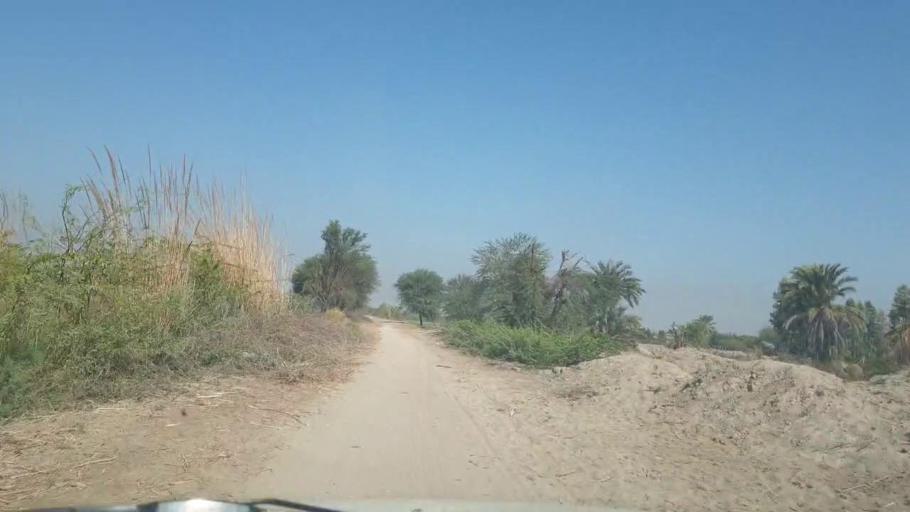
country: PK
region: Sindh
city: Mirpur Khas
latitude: 25.5159
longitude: 69.1623
